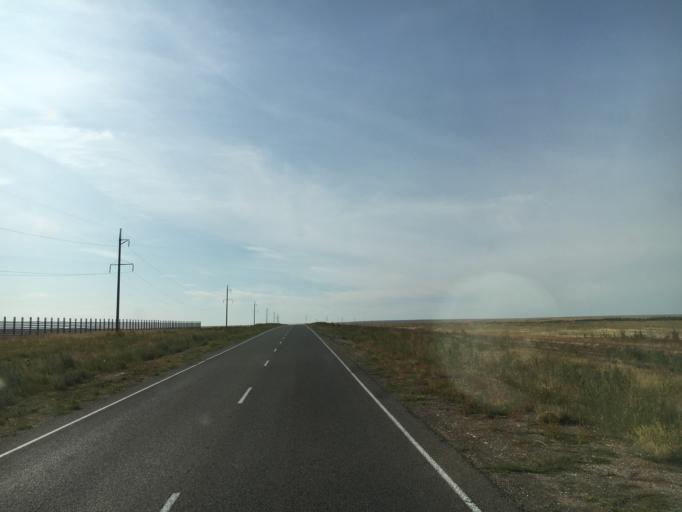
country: KZ
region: Batys Qazaqstan
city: Kamenka
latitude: 51.1440
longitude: 50.0961
